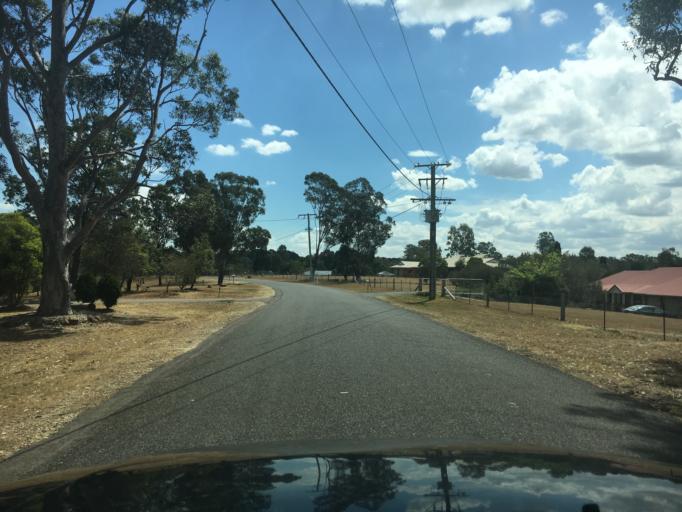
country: AU
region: New South Wales
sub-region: Singleton
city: Singleton
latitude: -32.5203
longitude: 151.1892
